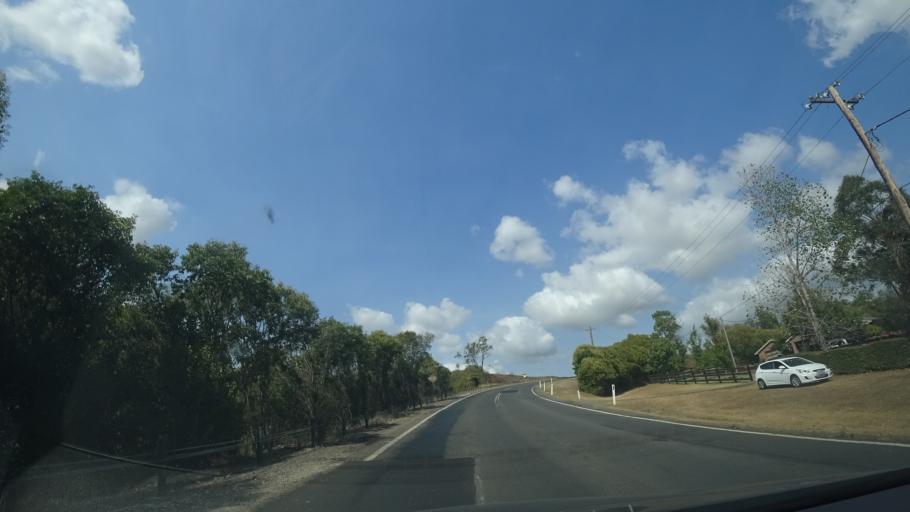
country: AU
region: New South Wales
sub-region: Wollondilly
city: Picton
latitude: -34.1860
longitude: 150.6037
